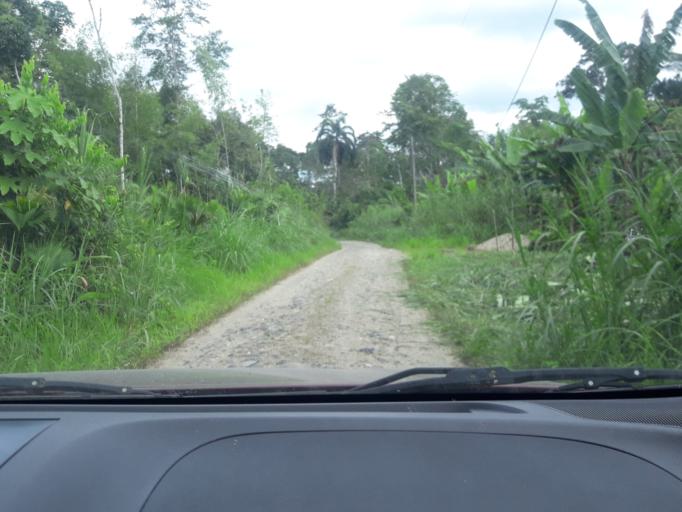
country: EC
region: Napo
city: Tena
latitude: -1.0966
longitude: -77.6803
